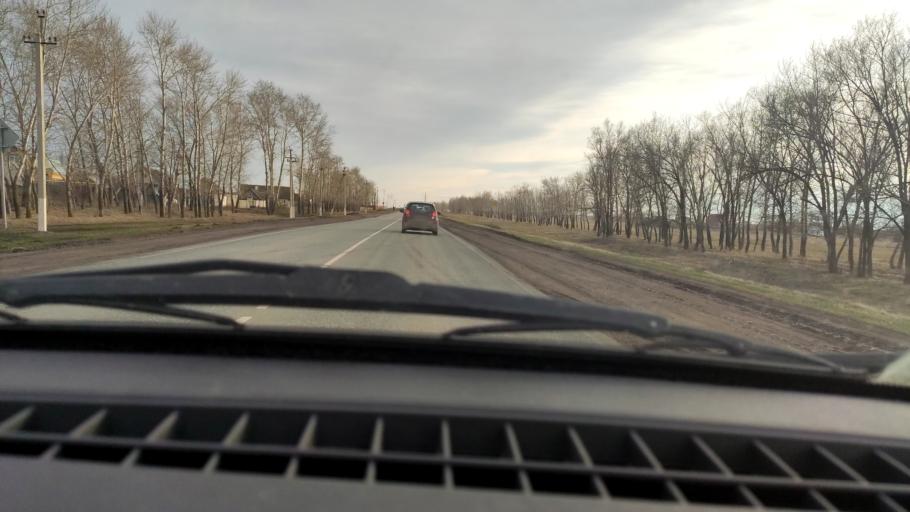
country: RU
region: Bashkortostan
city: Davlekanovo
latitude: 54.3905
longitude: 55.2026
